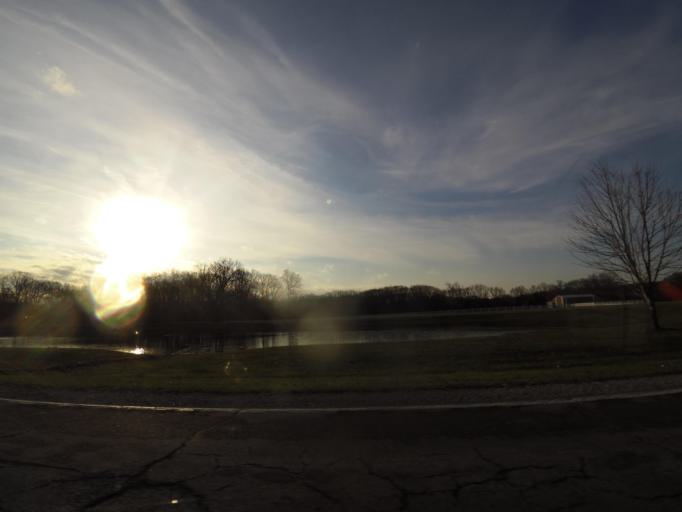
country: US
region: Illinois
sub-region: Bond County
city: Greenville
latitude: 38.9187
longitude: -89.2637
